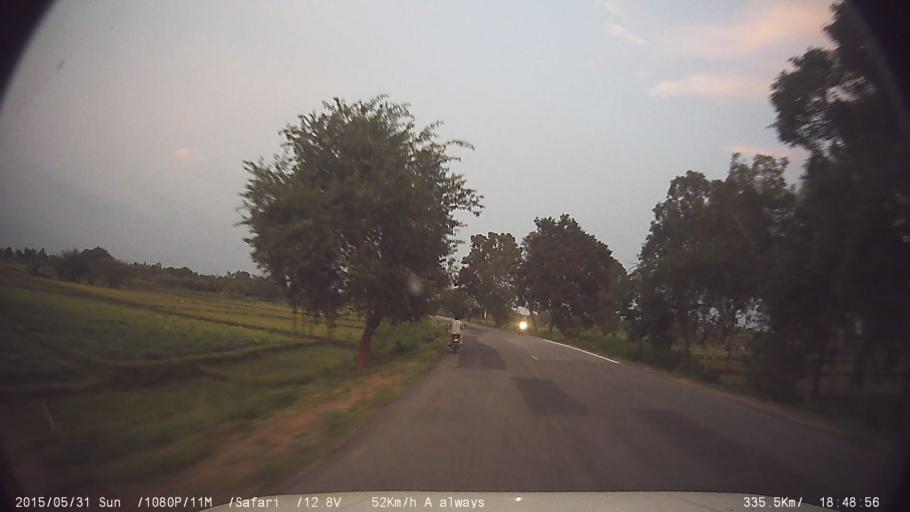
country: IN
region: Karnataka
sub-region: Mysore
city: Tirumakudal Narsipur
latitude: 12.1714
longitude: 76.8467
